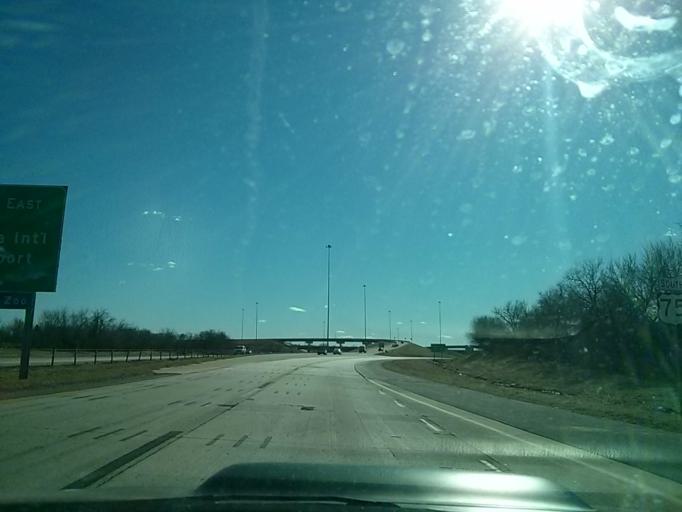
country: US
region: Oklahoma
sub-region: Tulsa County
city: Turley
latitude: 36.2052
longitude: -95.9473
